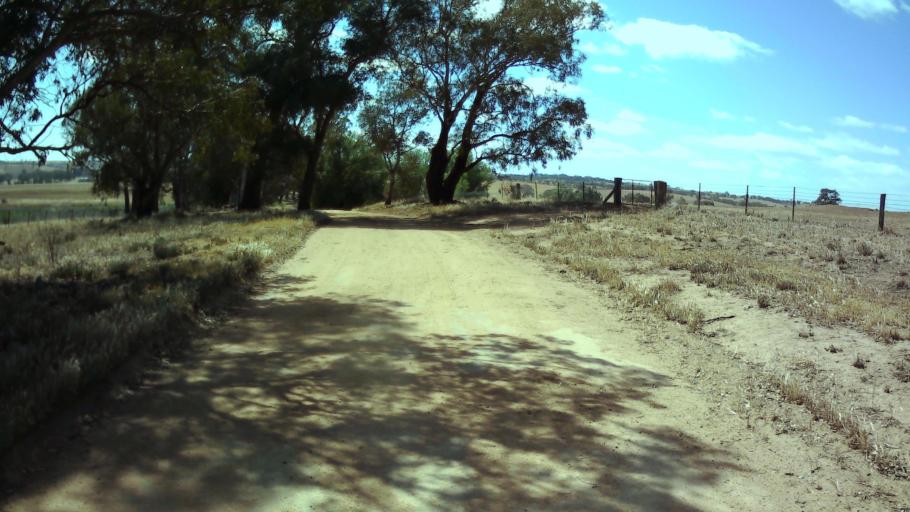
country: AU
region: New South Wales
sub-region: Weddin
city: Grenfell
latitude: -33.9558
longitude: 148.4224
